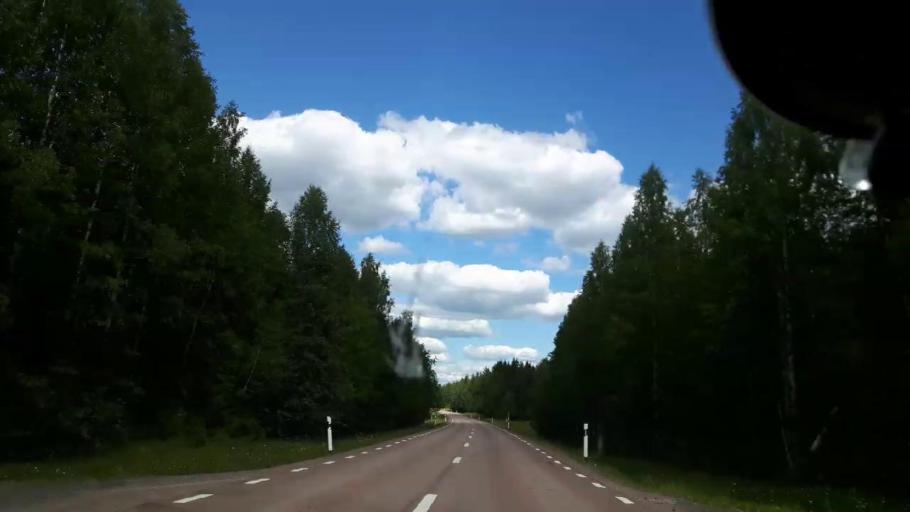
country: SE
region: Jaemtland
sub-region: Ragunda Kommun
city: Hammarstrand
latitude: 62.9052
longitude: 16.7011
